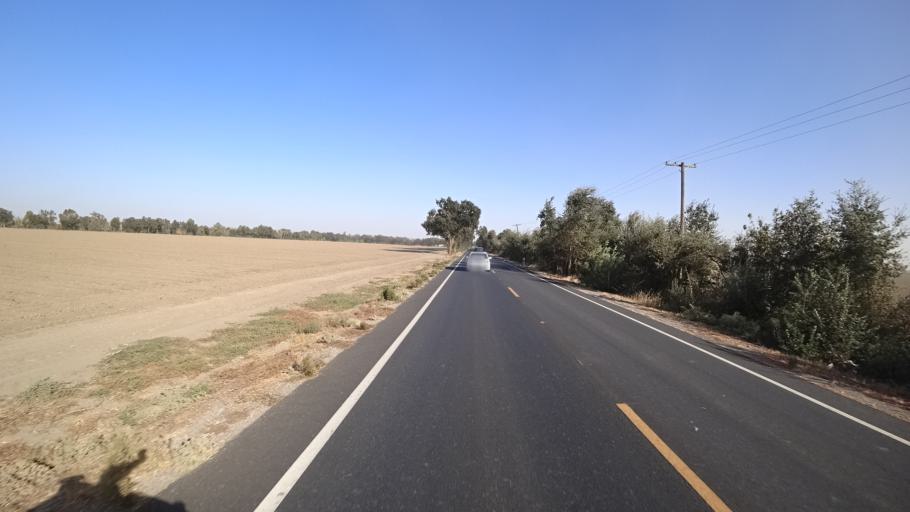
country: US
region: California
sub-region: Yolo County
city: Woodland
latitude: 38.7926
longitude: -121.7378
